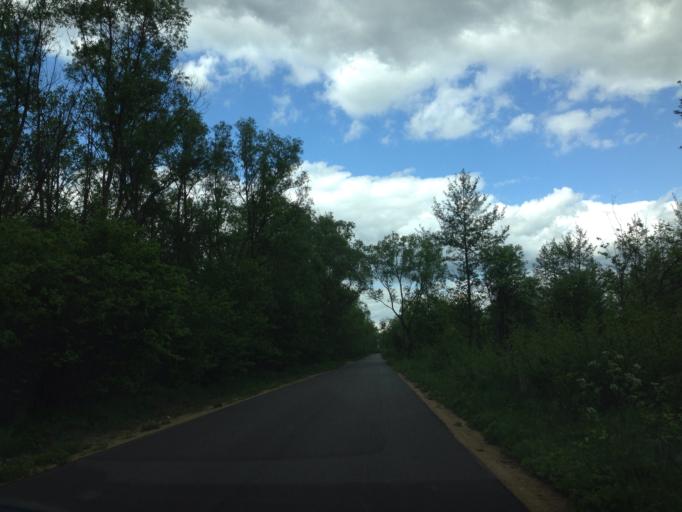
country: PL
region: Podlasie
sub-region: Powiat bialostocki
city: Tykocin
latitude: 53.3135
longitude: 22.6027
